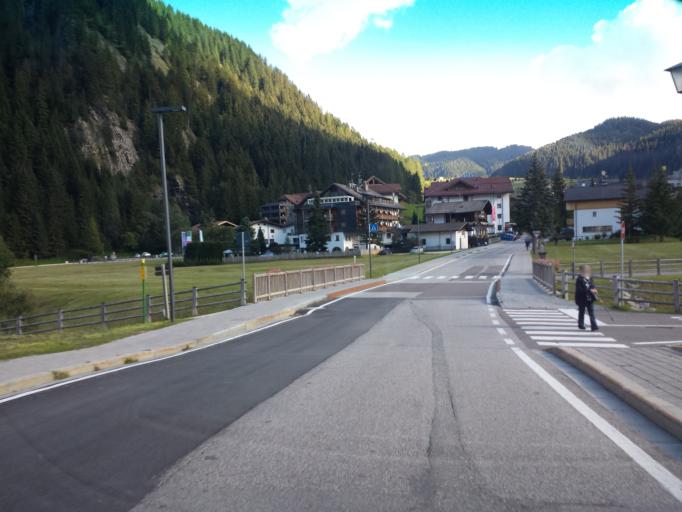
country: IT
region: Trentino-Alto Adige
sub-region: Bolzano
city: Corvara in Badia
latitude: 46.5541
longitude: 11.8726
